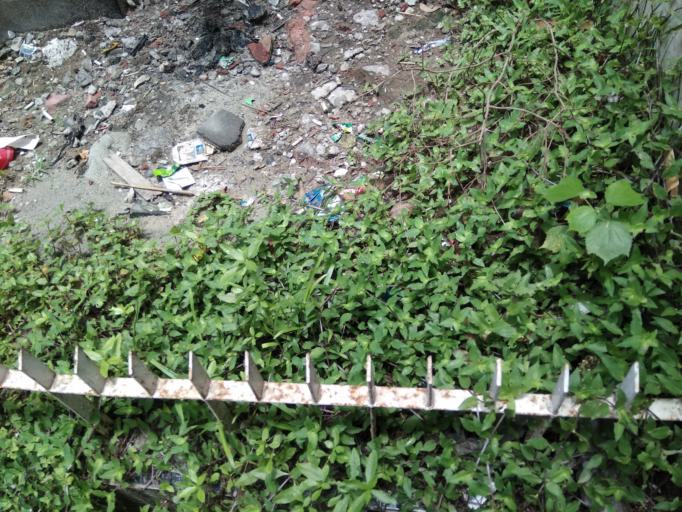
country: BD
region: Dhaka
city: Azimpur
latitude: 23.7979
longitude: 90.3703
